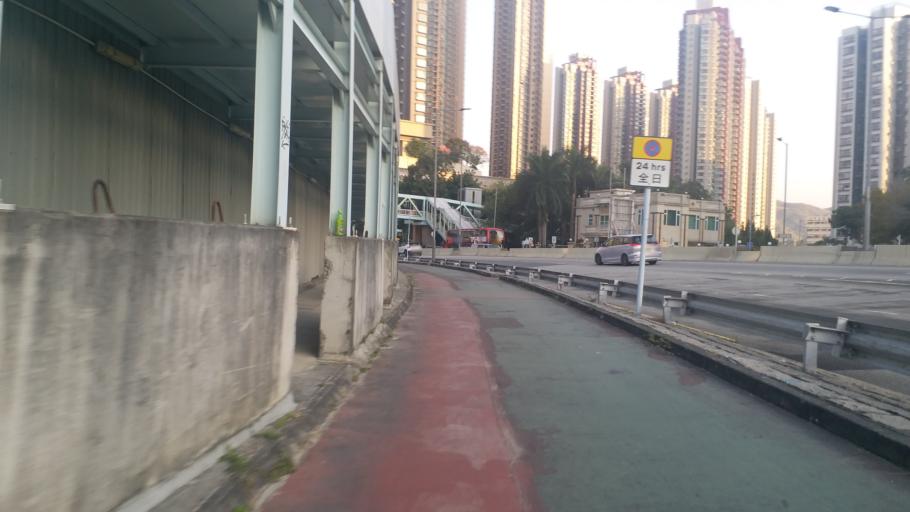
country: HK
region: Yuen Long
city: Yuen Long Kau Hui
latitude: 22.4447
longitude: 114.0337
